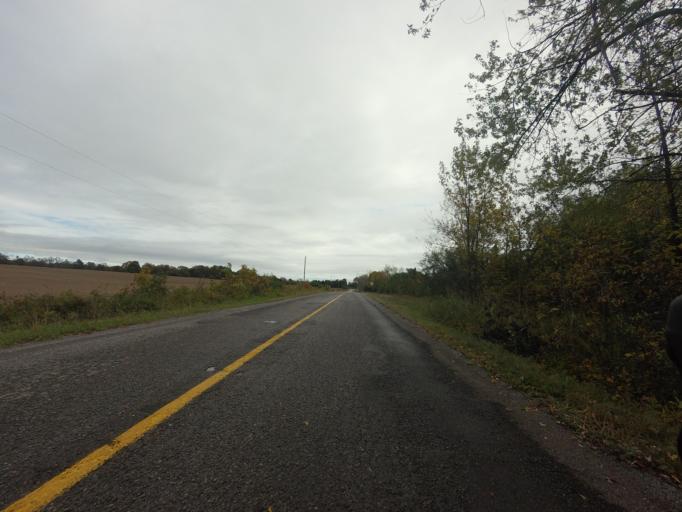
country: CA
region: Ontario
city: Cobourg
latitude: 43.9054
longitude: -78.5035
